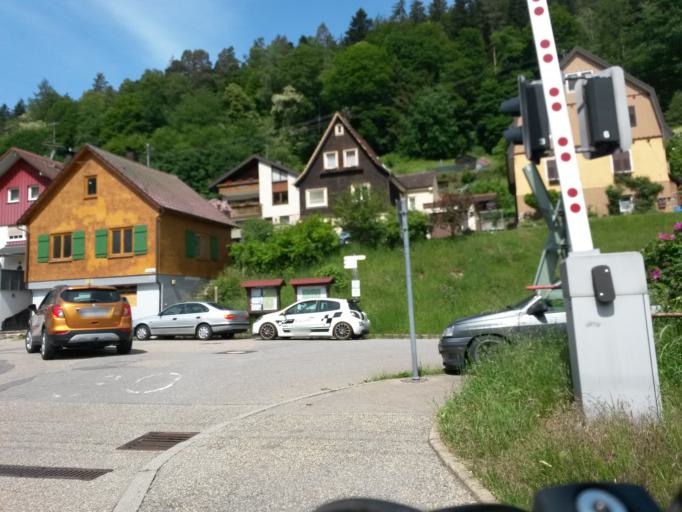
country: DE
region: Baden-Wuerttemberg
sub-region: Karlsruhe Region
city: Hofen an der Enz
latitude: 48.7752
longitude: 8.5691
